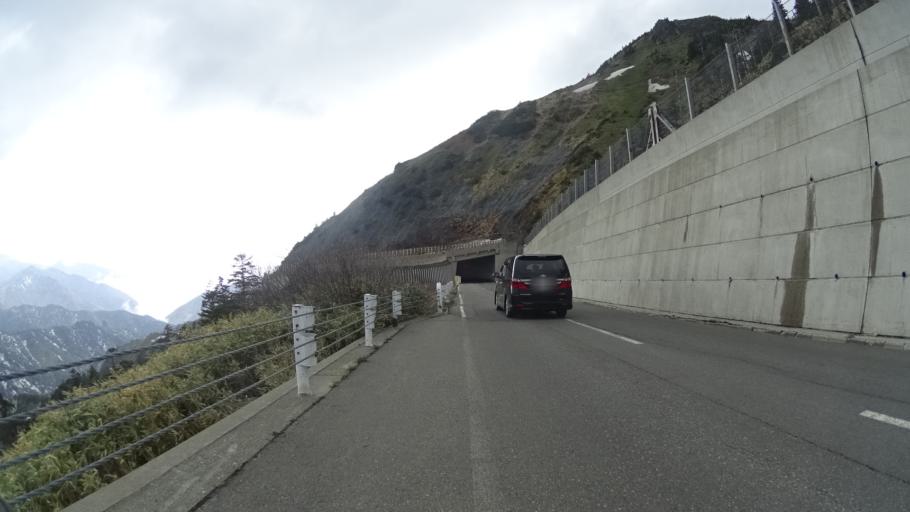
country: JP
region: Nagano
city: Nakano
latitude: 36.6662
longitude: 138.5278
